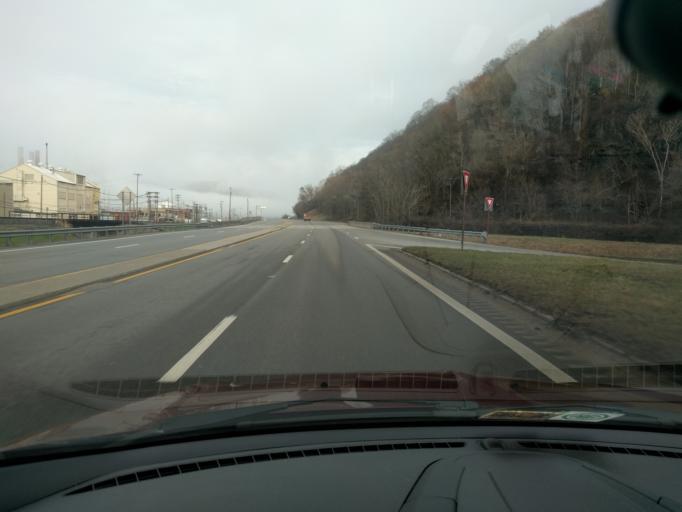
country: US
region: West Virginia
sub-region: Kanawha County
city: Belle
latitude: 38.2424
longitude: -81.5498
